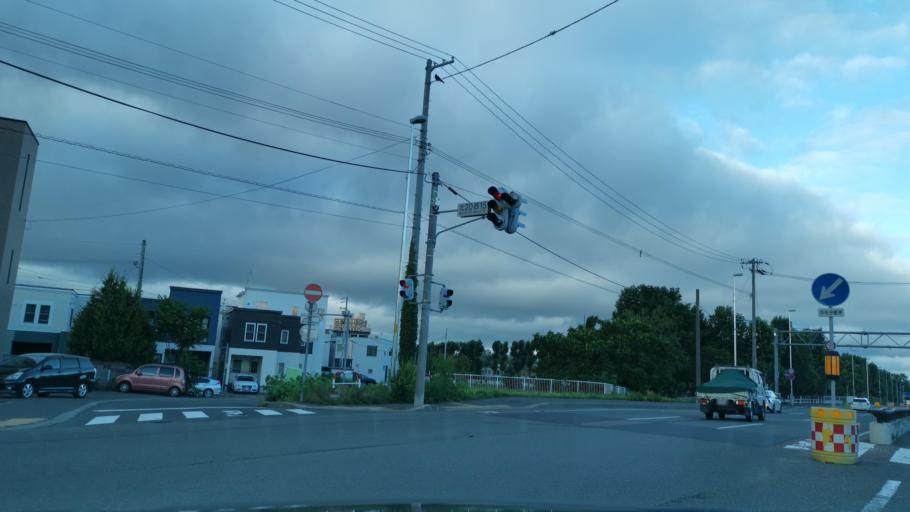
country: JP
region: Hokkaido
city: Sapporo
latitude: 43.0816
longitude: 141.3244
